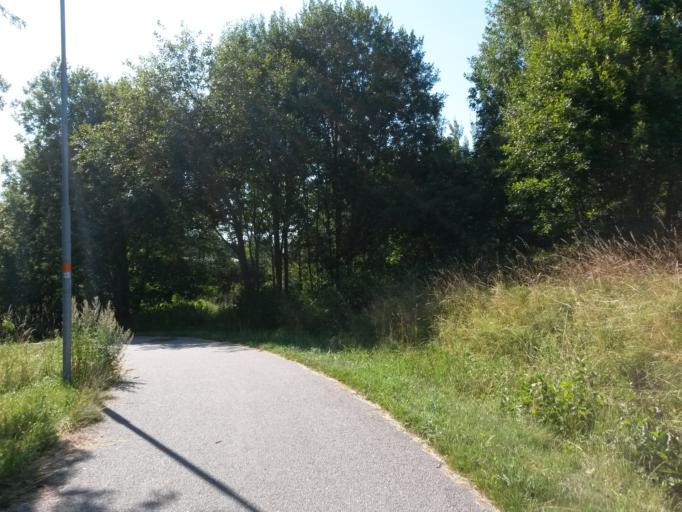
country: SE
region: Vaestra Goetaland
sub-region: Gotene Kommun
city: Kallby
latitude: 58.5058
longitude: 13.2975
